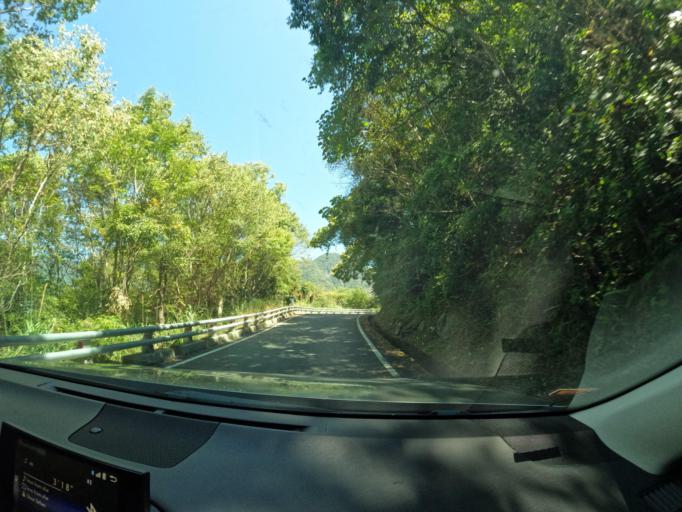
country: TW
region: Taiwan
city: Yujing
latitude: 23.2893
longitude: 120.8508
